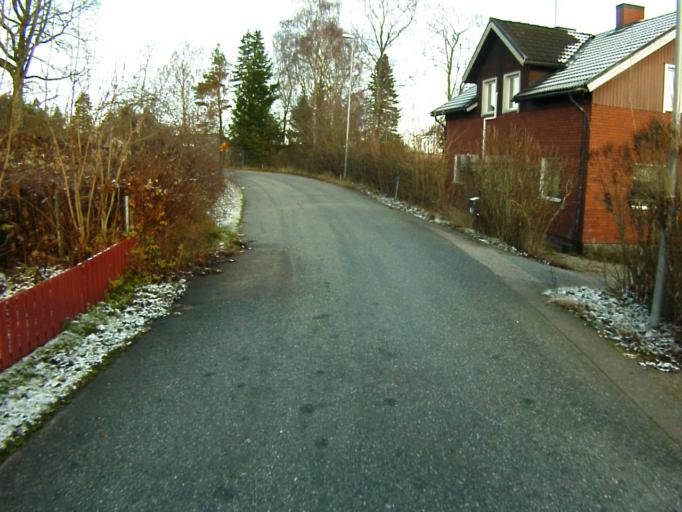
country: SE
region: Soedermanland
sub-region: Eskilstuna Kommun
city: Hallbybrunn
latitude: 59.3843
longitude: 16.4342
